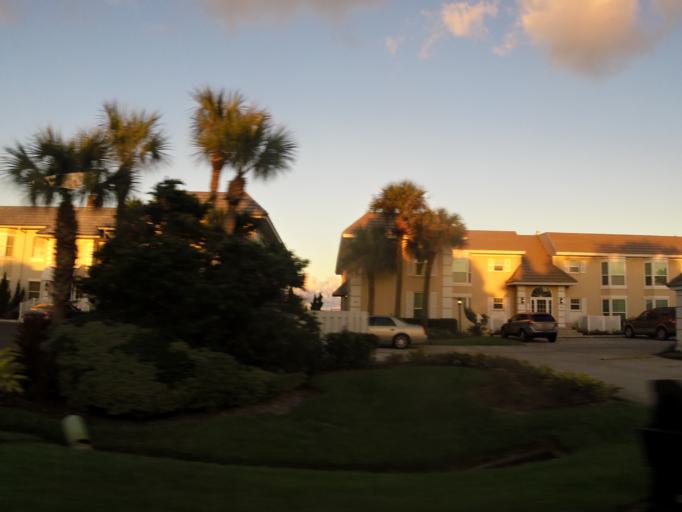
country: US
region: Florida
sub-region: Saint Johns County
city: Sawgrass
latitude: 30.2113
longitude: -81.3701
